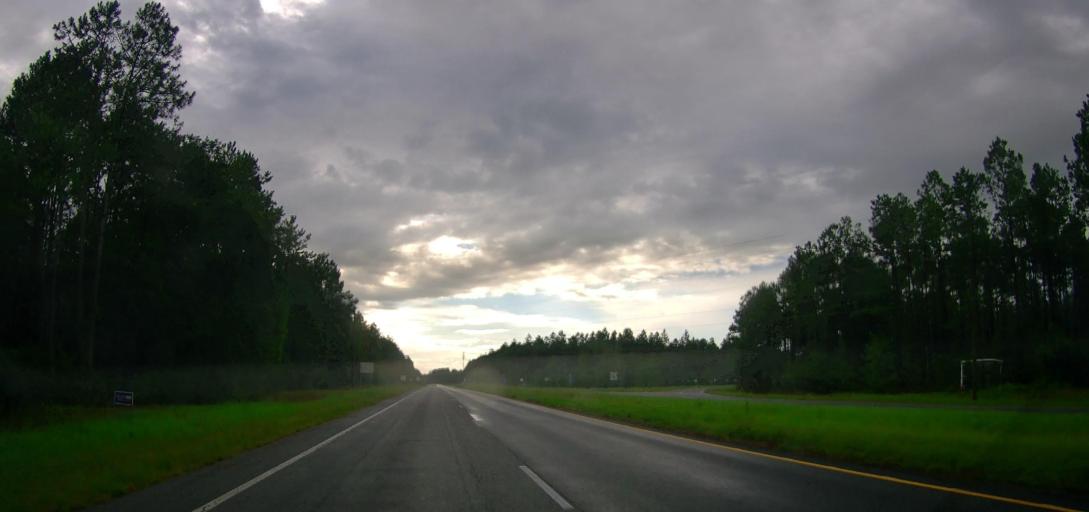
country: US
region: Georgia
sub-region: Ware County
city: Deenwood
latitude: 31.2615
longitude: -82.5157
